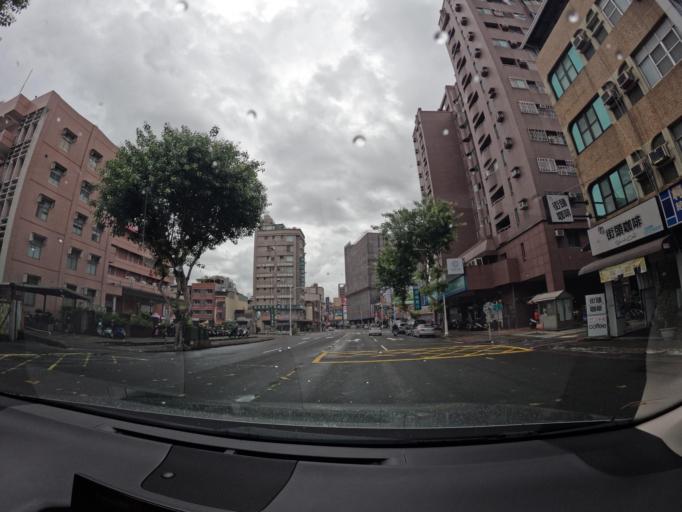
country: TW
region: Kaohsiung
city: Kaohsiung
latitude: 22.6330
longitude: 120.3234
